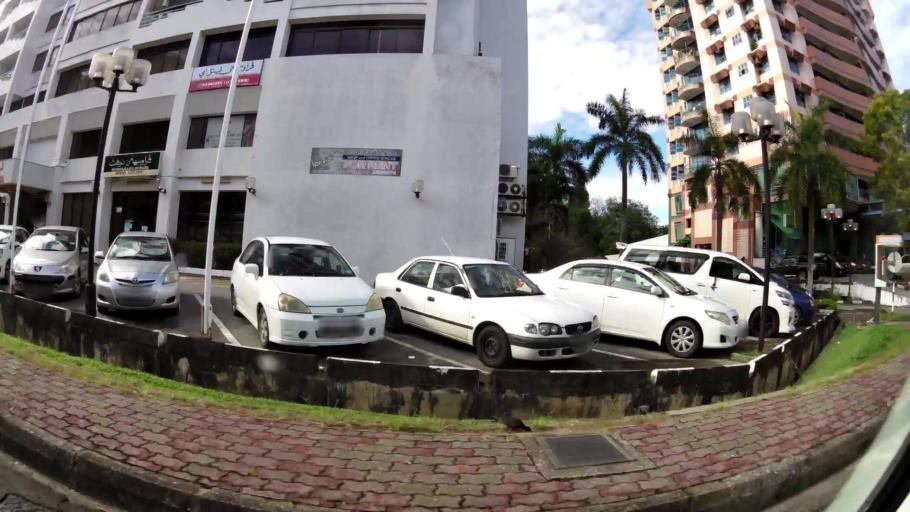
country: BN
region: Brunei and Muara
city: Bandar Seri Begawan
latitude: 4.8916
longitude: 114.9456
